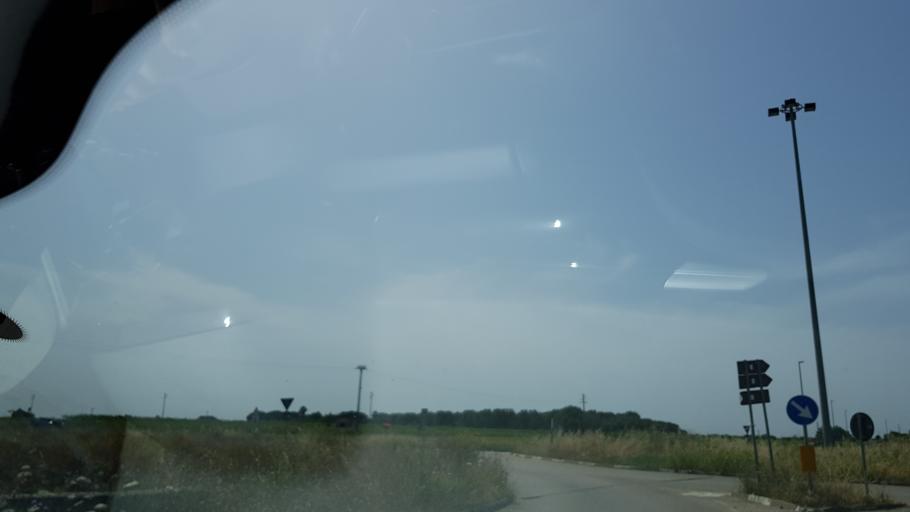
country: IT
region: Apulia
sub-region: Provincia di Brindisi
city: Mesagne
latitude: 40.5514
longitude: 17.8329
